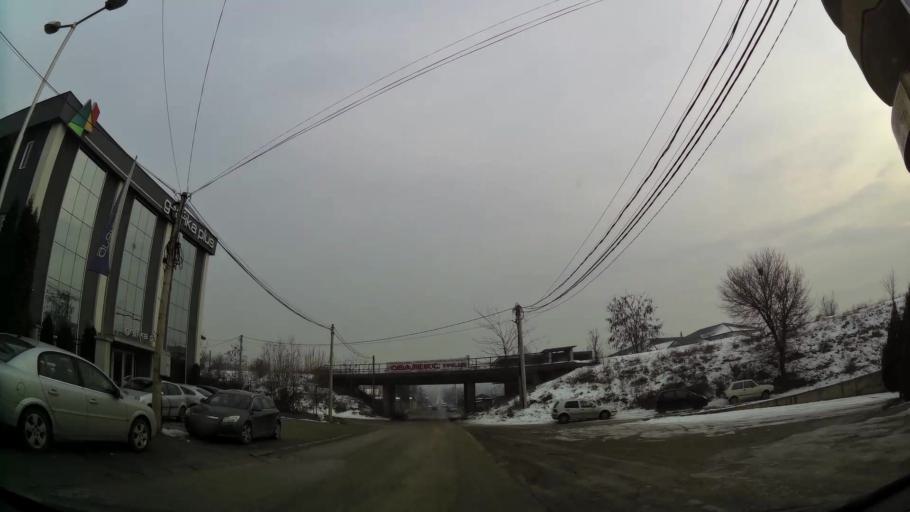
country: MK
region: Suto Orizari
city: Suto Orizare
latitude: 42.0275
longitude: 21.4097
